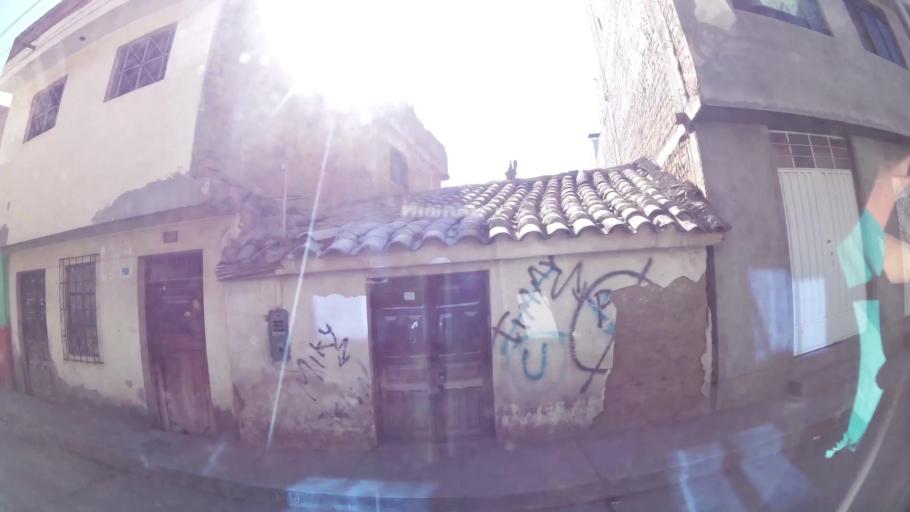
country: PE
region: Ayacucho
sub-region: Provincia de Huamanga
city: Ayacucho
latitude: -13.1623
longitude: -74.2340
